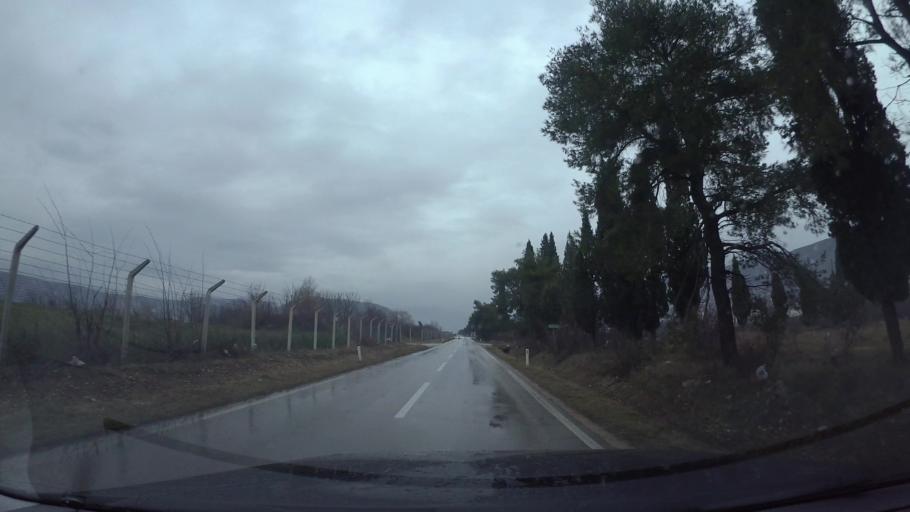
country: BA
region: Federation of Bosnia and Herzegovina
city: Rodoc
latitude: 43.2938
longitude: 17.8450
